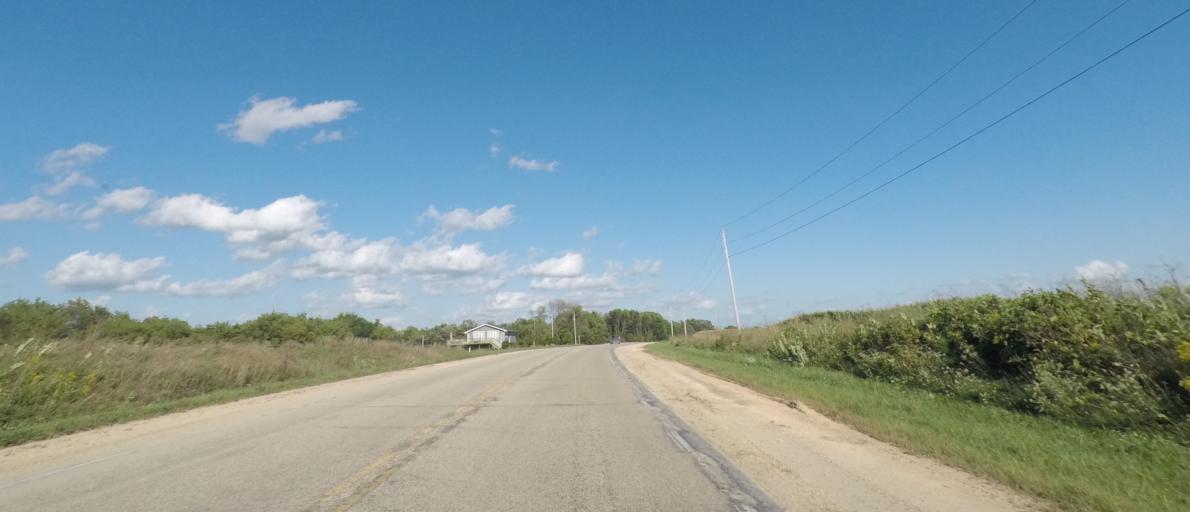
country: US
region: Wisconsin
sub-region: Iowa County
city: Dodgeville
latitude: 42.9797
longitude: -90.0623
